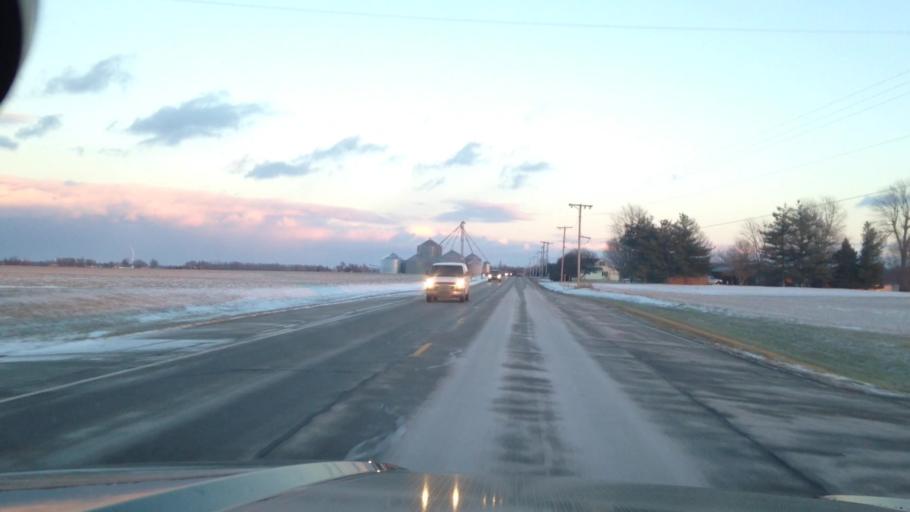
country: US
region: Indiana
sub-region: Randolph County
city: Union City
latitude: 40.1783
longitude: -84.8578
